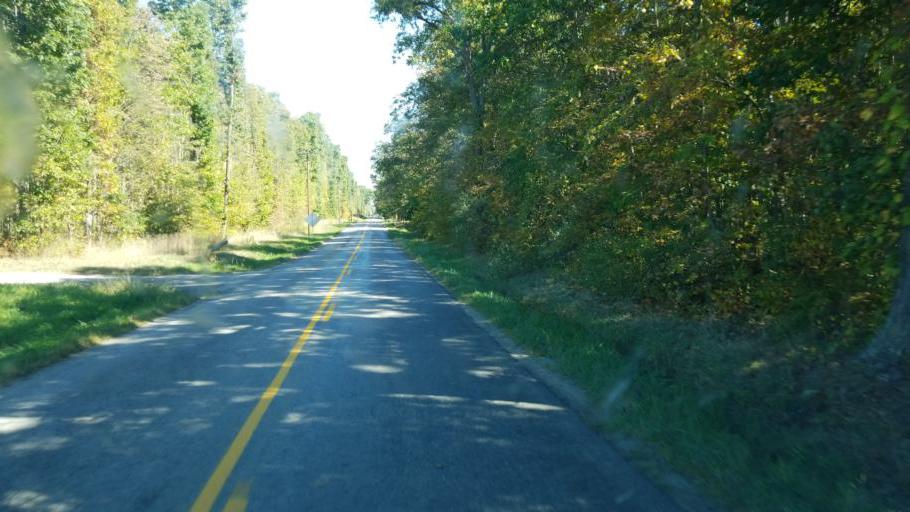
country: US
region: Ohio
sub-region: Huron County
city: New London
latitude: 40.9929
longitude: -82.4171
